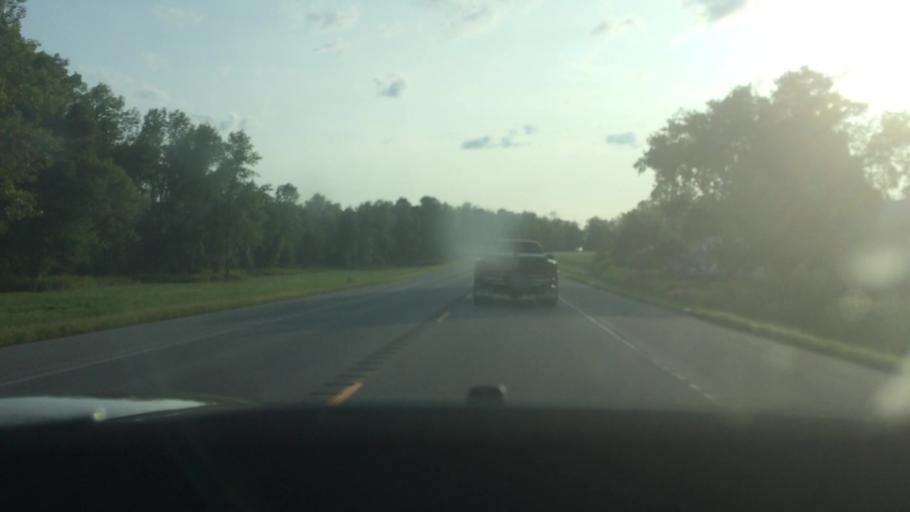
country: US
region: New York
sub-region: St. Lawrence County
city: Ogdensburg
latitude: 44.6800
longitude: -75.4992
